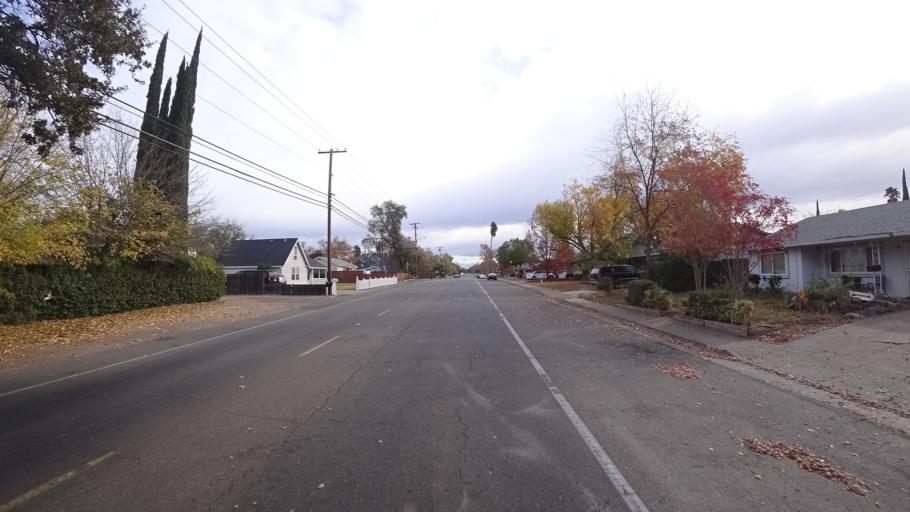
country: US
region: California
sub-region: Sacramento County
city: Citrus Heights
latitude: 38.7004
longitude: -121.2674
